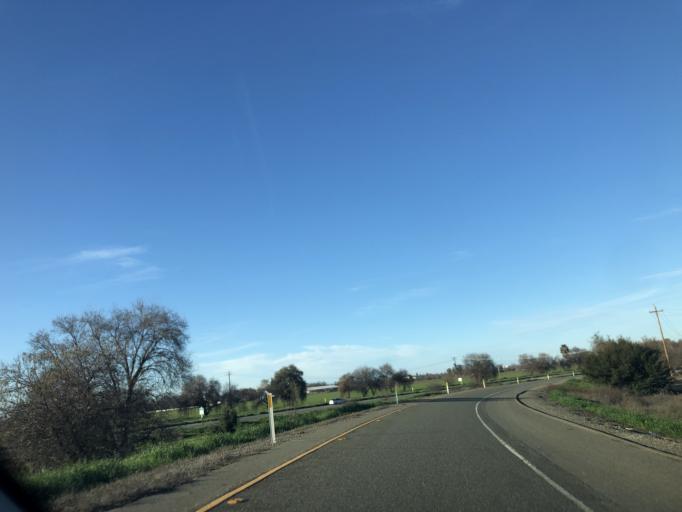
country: US
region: California
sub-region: Yolo County
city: Woodland
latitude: 38.6416
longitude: -121.7582
